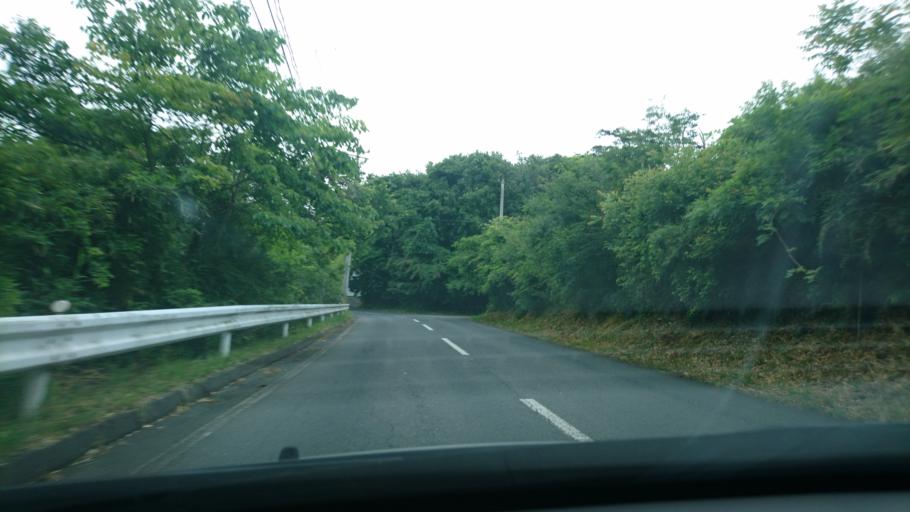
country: JP
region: Iwate
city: Ichinoseki
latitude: 38.9010
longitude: 141.1553
